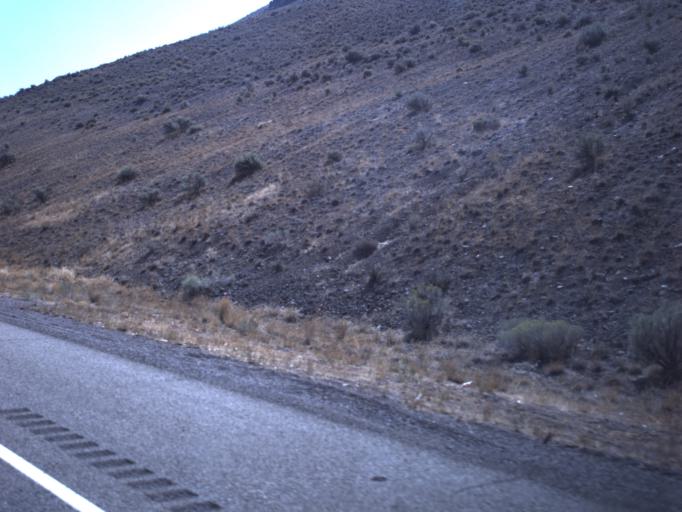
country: US
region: Utah
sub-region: Sevier County
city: Aurora
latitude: 38.8786
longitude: -111.9371
